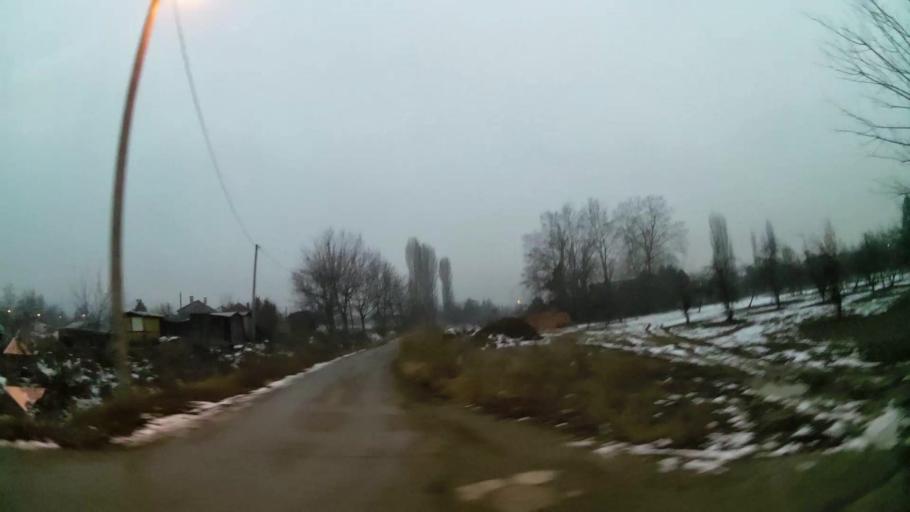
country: MK
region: Kisela Voda
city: Kisela Voda
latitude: 41.9721
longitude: 21.4918
